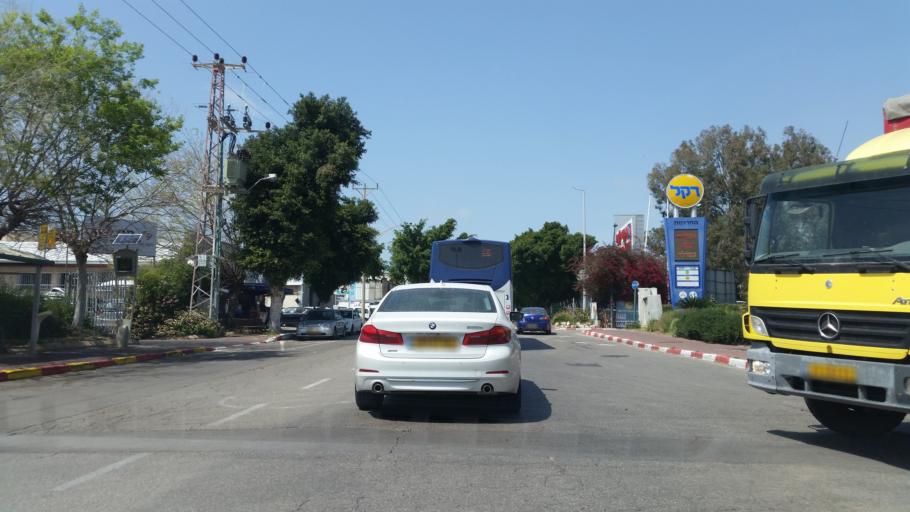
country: IL
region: Central District
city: Ra'anana
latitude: 32.1935
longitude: 34.8809
